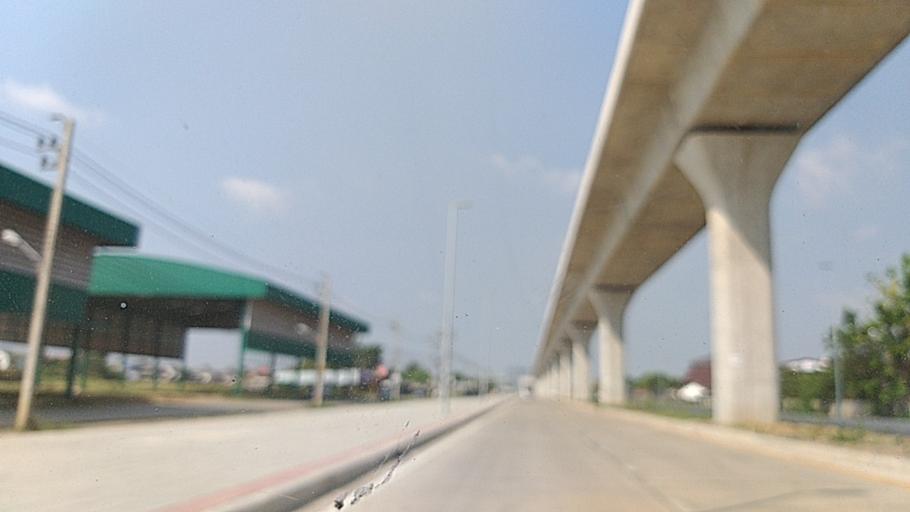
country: TH
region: Bangkok
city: Sai Mai
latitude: 13.9299
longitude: 100.6340
